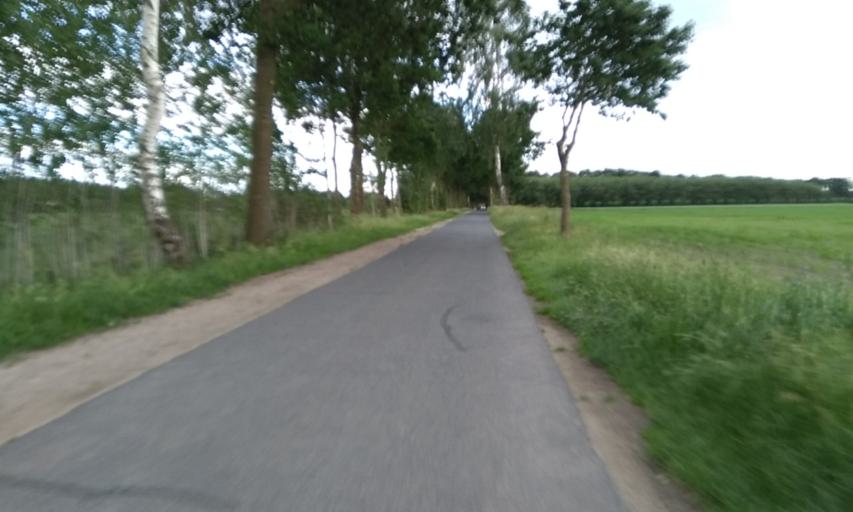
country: DE
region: Lower Saxony
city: Regesbostel
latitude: 53.3865
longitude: 9.6437
